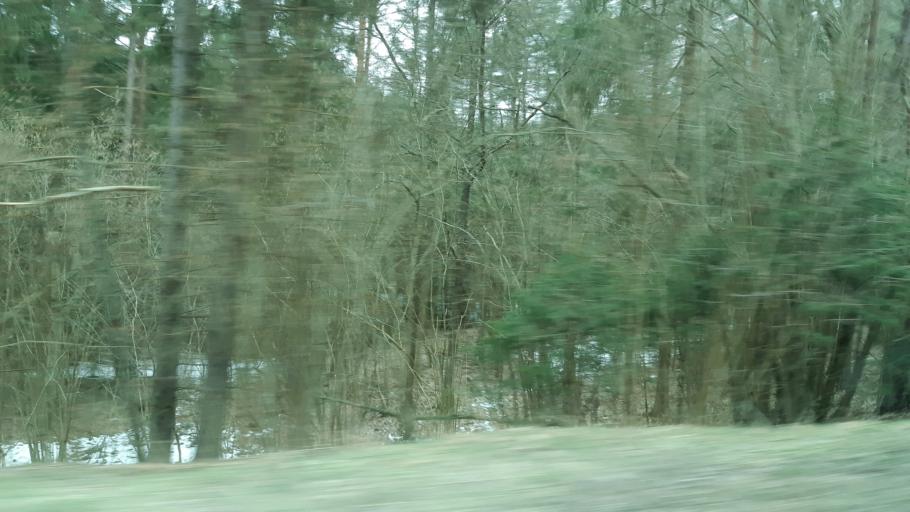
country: PL
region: Podlasie
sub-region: Suwalki
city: Suwalki
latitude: 54.2860
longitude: 22.9527
